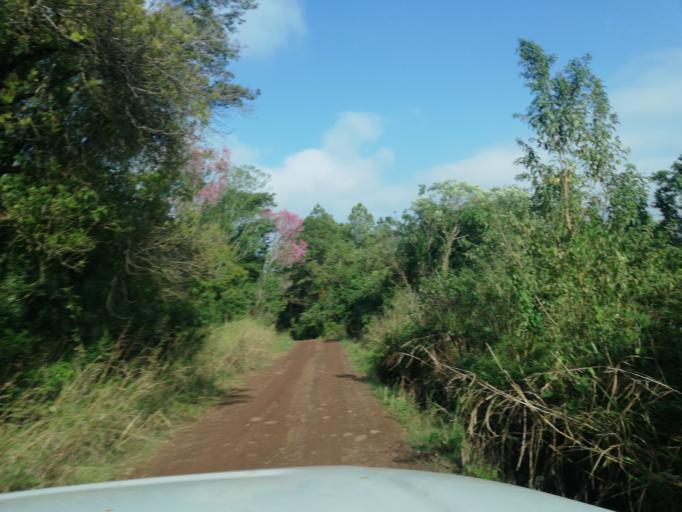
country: AR
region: Misiones
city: Cerro Azul
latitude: -27.5794
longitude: -55.5126
